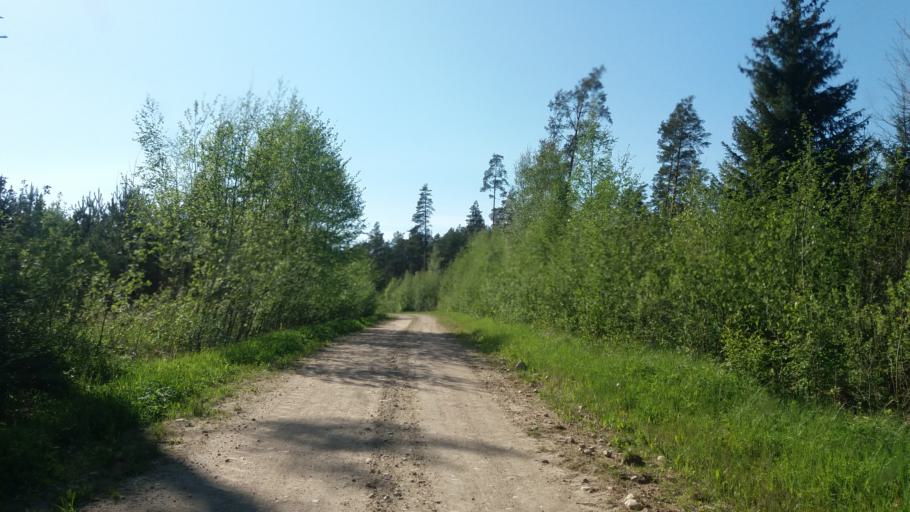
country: LV
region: Talsu Rajons
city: Stende
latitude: 57.0495
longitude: 22.2931
